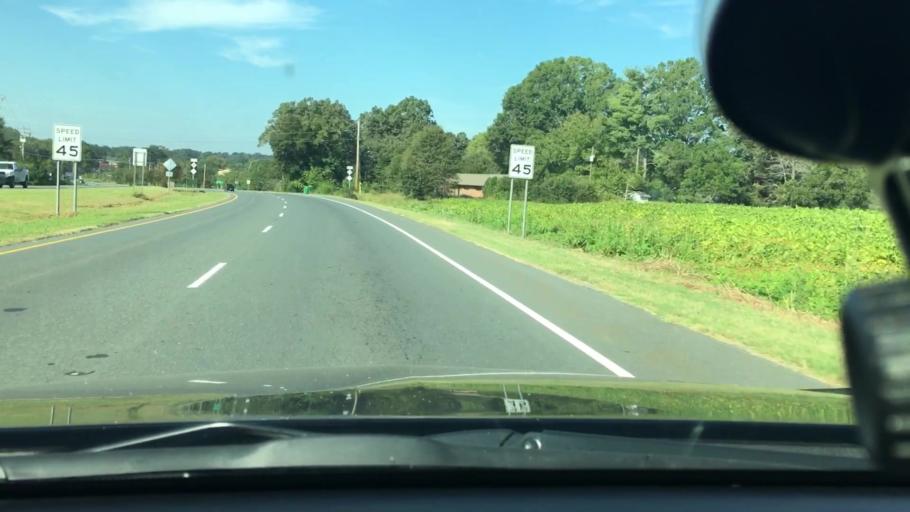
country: US
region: North Carolina
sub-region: Stanly County
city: Albemarle
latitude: 35.3343
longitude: -80.2287
